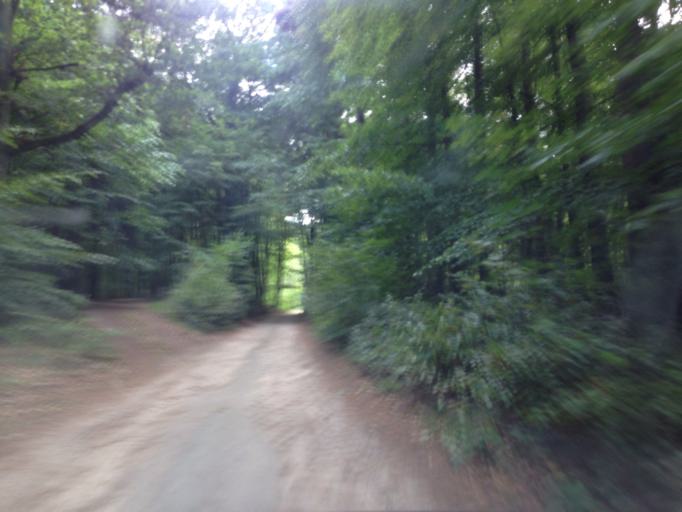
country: PL
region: Warmian-Masurian Voivodeship
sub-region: Powiat ilawski
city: Susz
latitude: 53.7702
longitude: 19.3217
